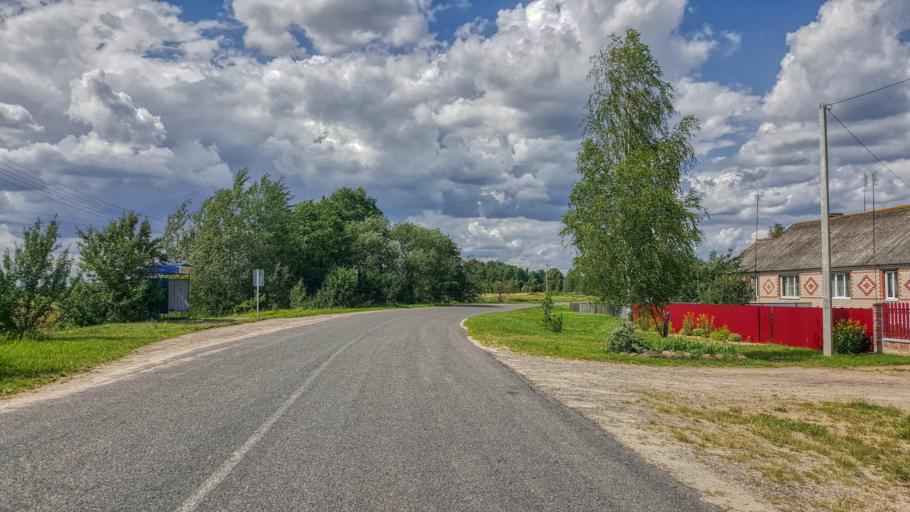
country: BY
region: Brest
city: Kamyanyets
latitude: 52.4148
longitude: 23.8883
